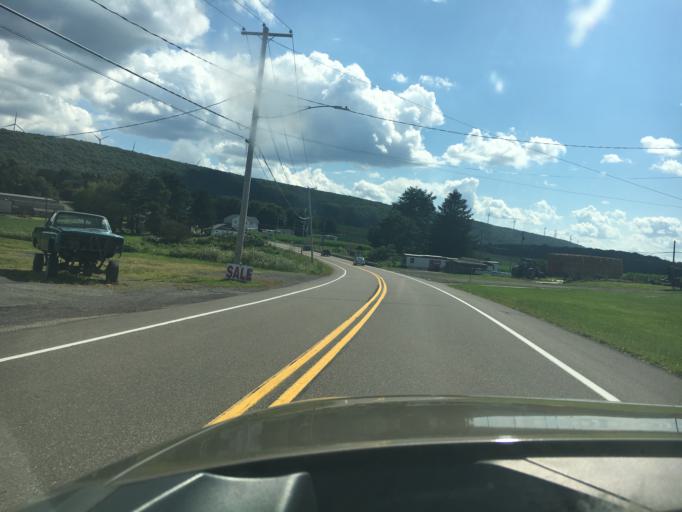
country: US
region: Pennsylvania
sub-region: Schuylkill County
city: Shenandoah Heights
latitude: 40.8673
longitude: -76.1656
